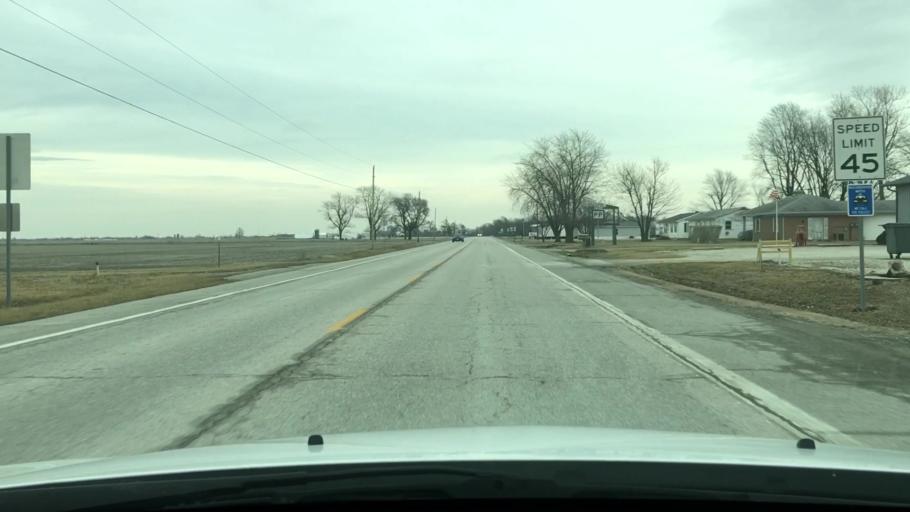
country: US
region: Missouri
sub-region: Audrain County
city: Vandalia
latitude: 39.2792
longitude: -91.5756
